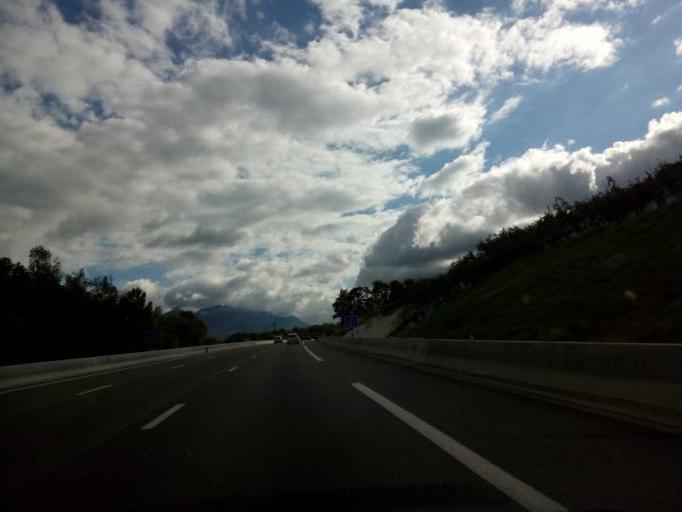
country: FR
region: Rhone-Alpes
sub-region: Departement de la Savoie
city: La Motte-Servolex
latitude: 45.5889
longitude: 5.8561
